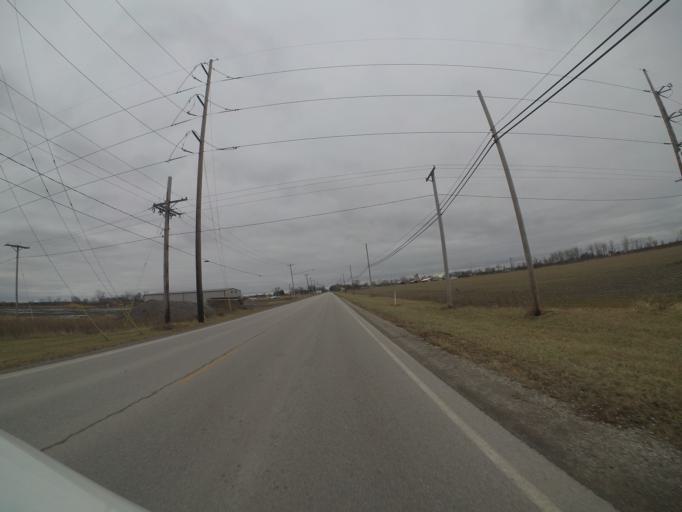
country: US
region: Ohio
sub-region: Wood County
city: Walbridge
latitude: 41.5926
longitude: -83.5127
